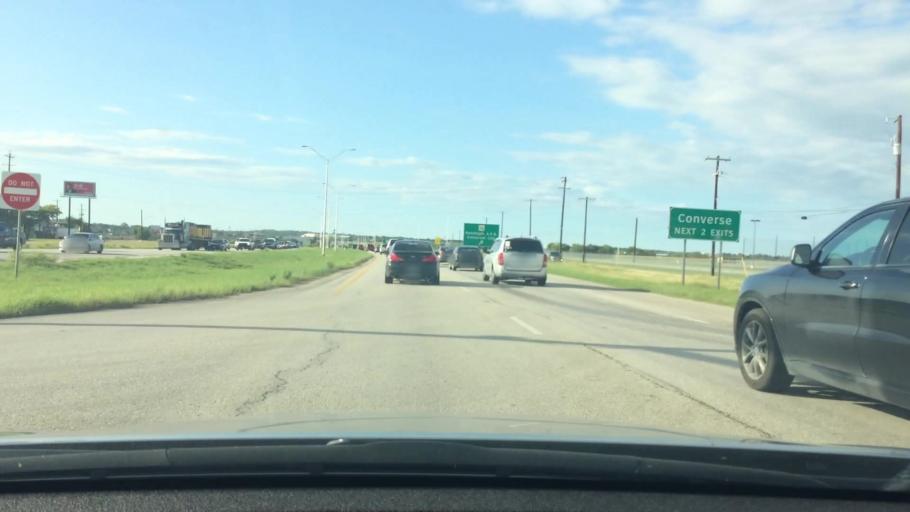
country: US
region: Texas
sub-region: Bexar County
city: Converse
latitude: 29.5277
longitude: -98.2973
